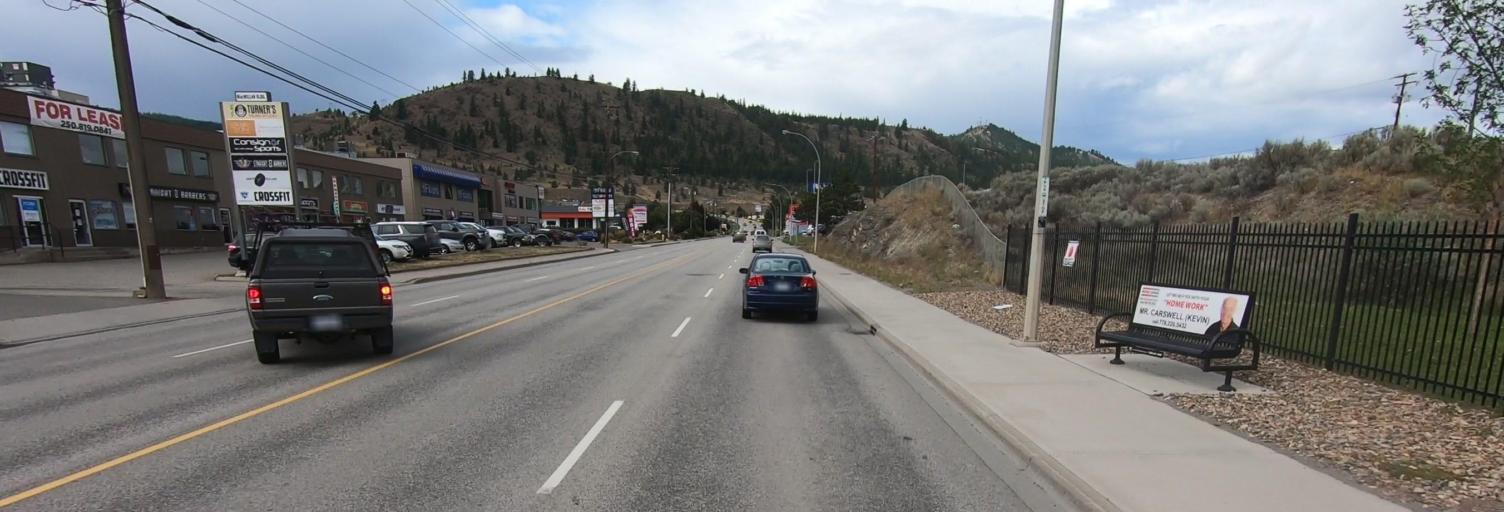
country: CA
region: British Columbia
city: Kamloops
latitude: 50.6636
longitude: -120.3594
